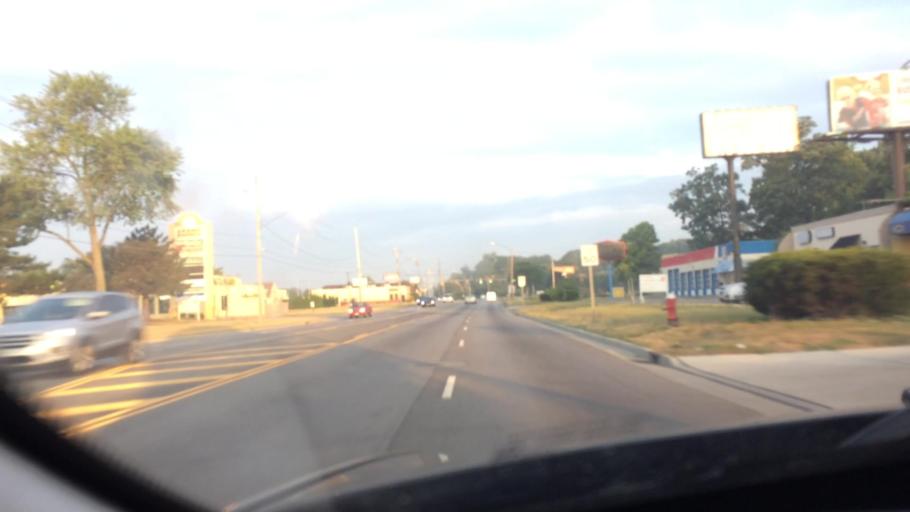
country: US
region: Ohio
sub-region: Lucas County
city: Holland
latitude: 41.6167
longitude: -83.6662
